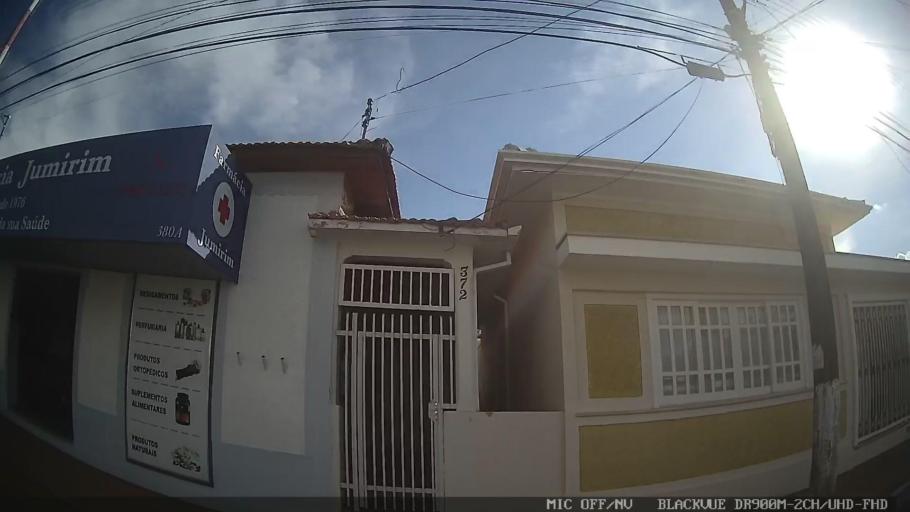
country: BR
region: Sao Paulo
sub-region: Laranjal Paulista
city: Laranjal Paulista
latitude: -23.0841
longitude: -47.7881
